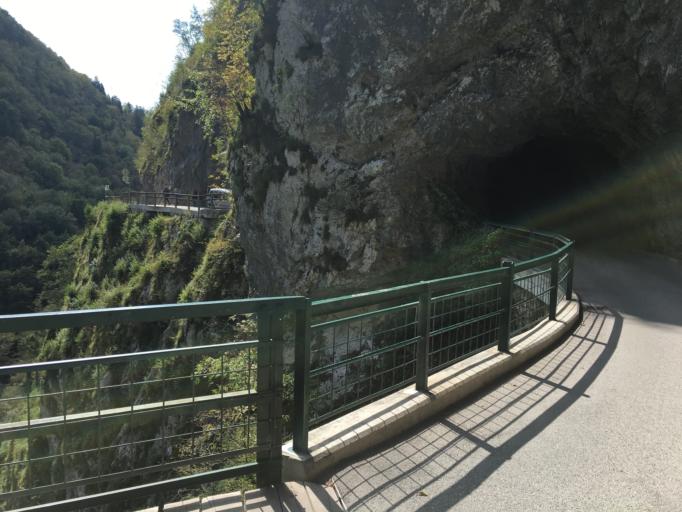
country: SI
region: Tolmin
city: Tolmin
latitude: 46.2014
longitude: 13.7421
